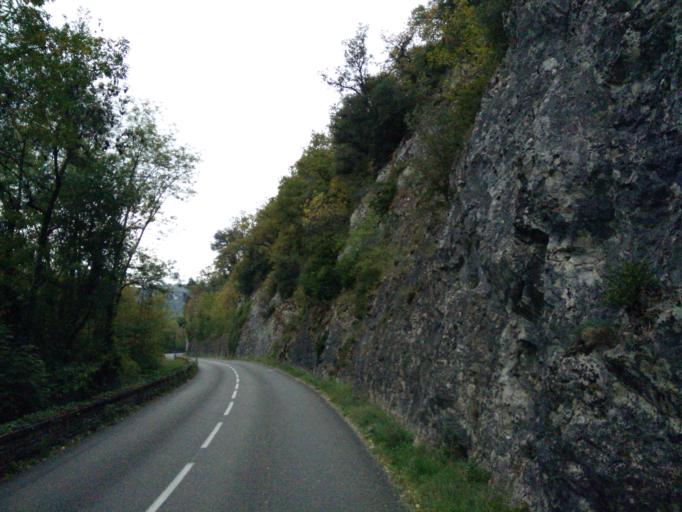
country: FR
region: Midi-Pyrenees
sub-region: Departement du Lot
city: Cahors
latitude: 44.4760
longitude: 1.5716
